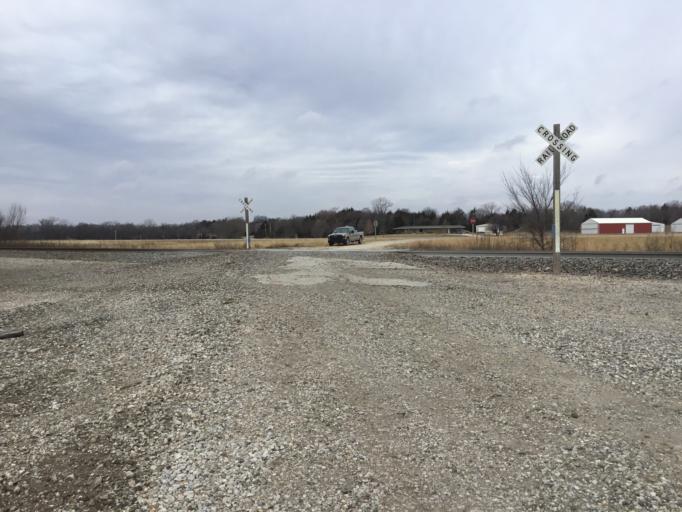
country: US
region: Kansas
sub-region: Chase County
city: Cottonwood Falls
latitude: 38.3047
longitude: -96.7342
